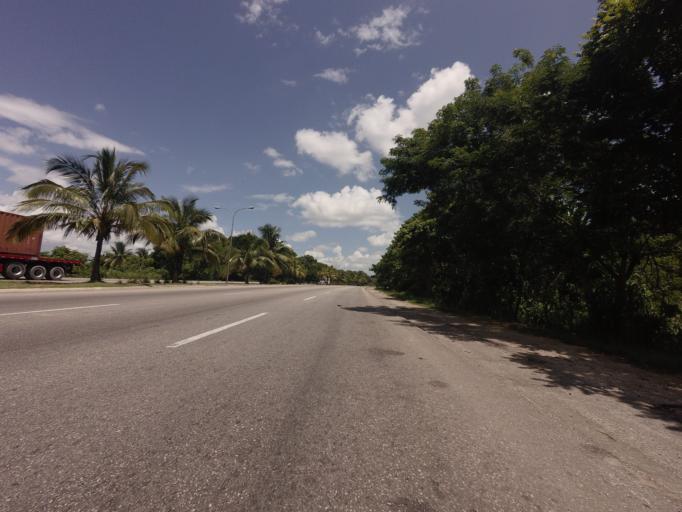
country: CU
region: La Habana
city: Arroyo Naranjo
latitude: 23.0450
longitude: -82.3738
